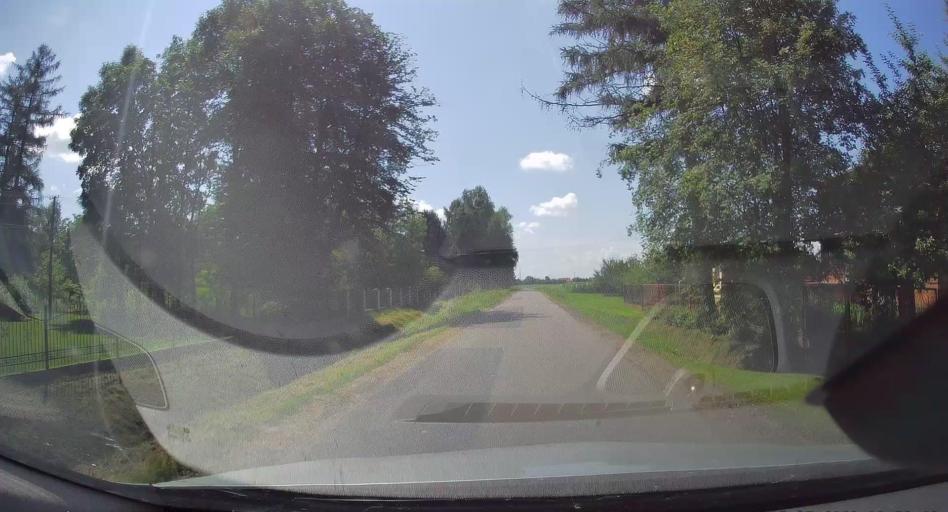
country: PL
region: Subcarpathian Voivodeship
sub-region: Powiat jaroslawski
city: Sosnica
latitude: 49.8747
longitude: 22.8593
